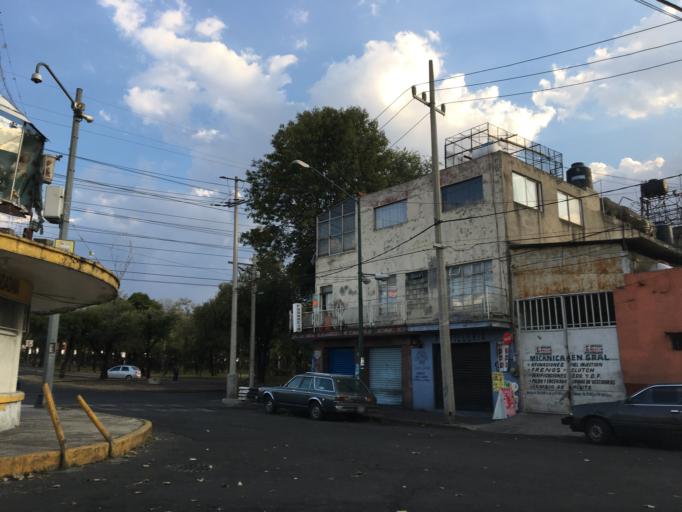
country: MX
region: Mexico City
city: Cuauhtemoc
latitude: 19.4625
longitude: -99.1455
